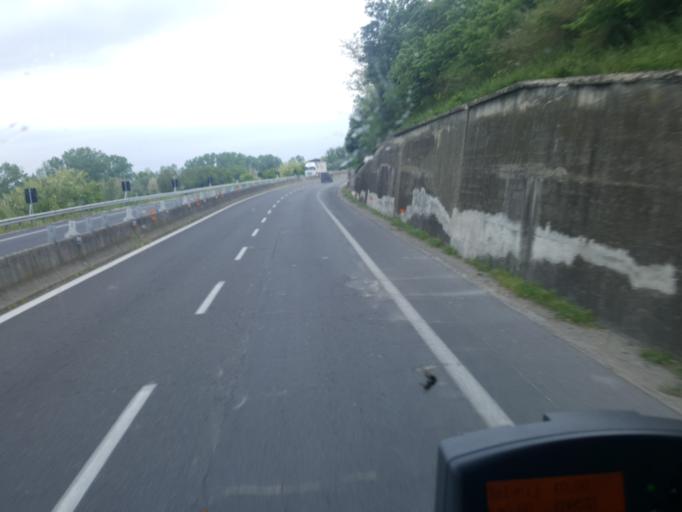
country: IT
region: Umbria
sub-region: Provincia di Perugia
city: Collepepe
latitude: 42.9212
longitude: 12.3918
